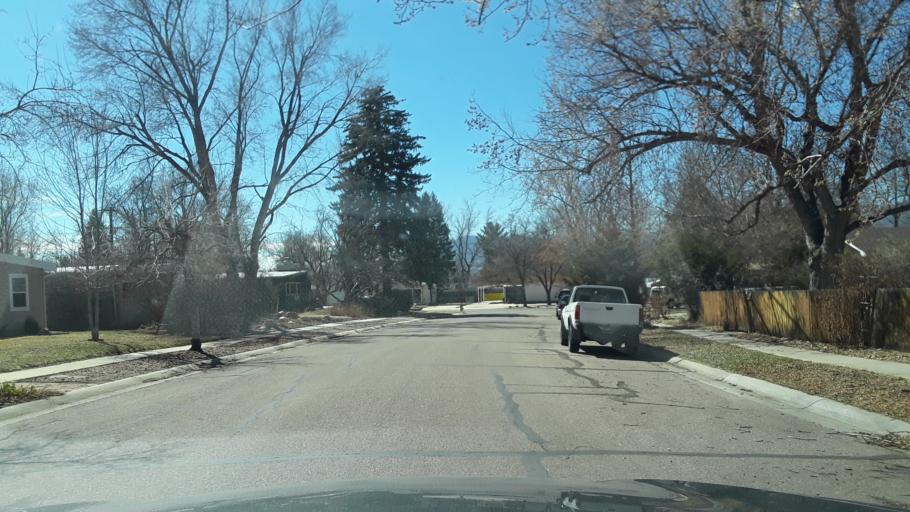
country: US
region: Colorado
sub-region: El Paso County
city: Colorado Springs
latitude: 38.8706
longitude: -104.8047
